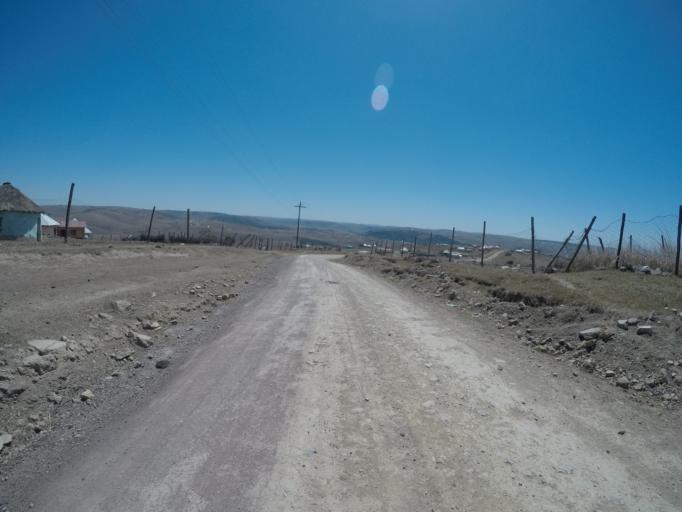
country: ZA
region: Eastern Cape
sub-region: OR Tambo District Municipality
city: Mthatha
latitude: -31.8870
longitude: 28.8757
